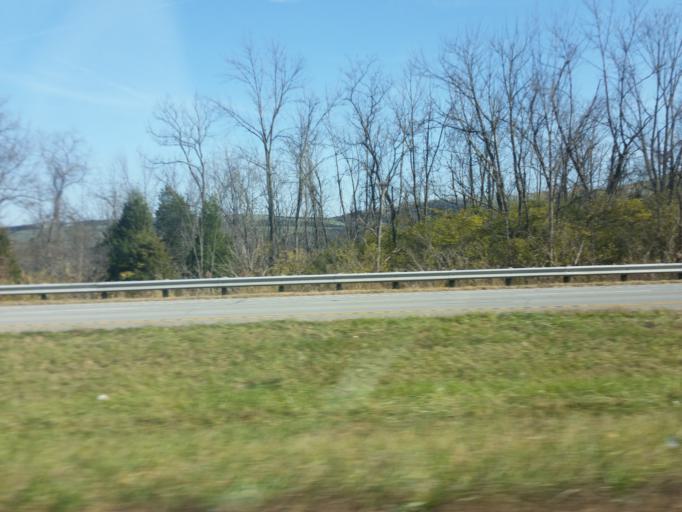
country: US
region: Ohio
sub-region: Hamilton County
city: Dunlap
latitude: 39.2823
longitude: -84.6050
